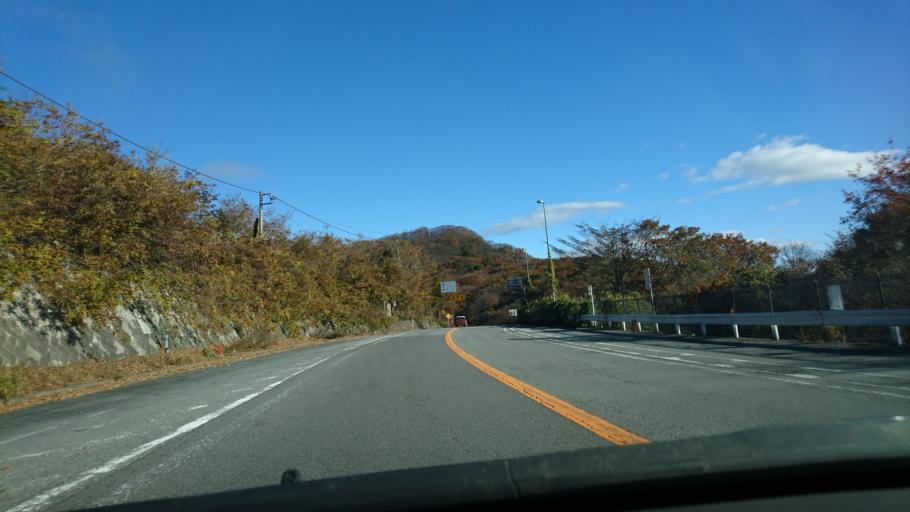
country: JP
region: Nagano
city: Saku
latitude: 36.3188
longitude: 138.6498
